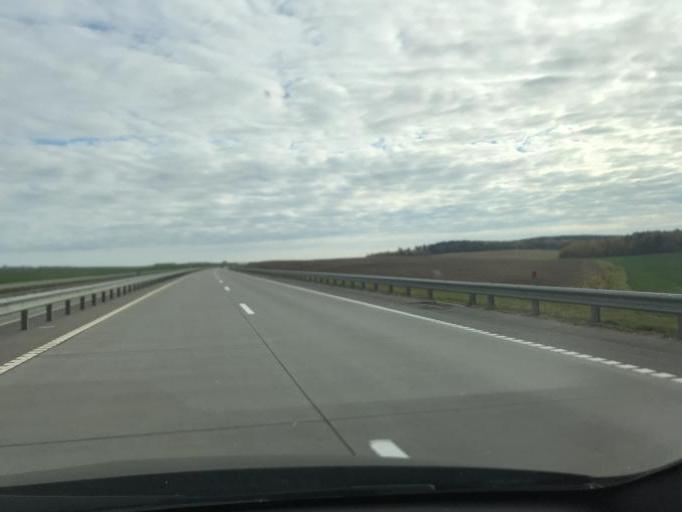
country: BY
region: Minsk
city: Syomkava
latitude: 54.0673
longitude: 27.4737
